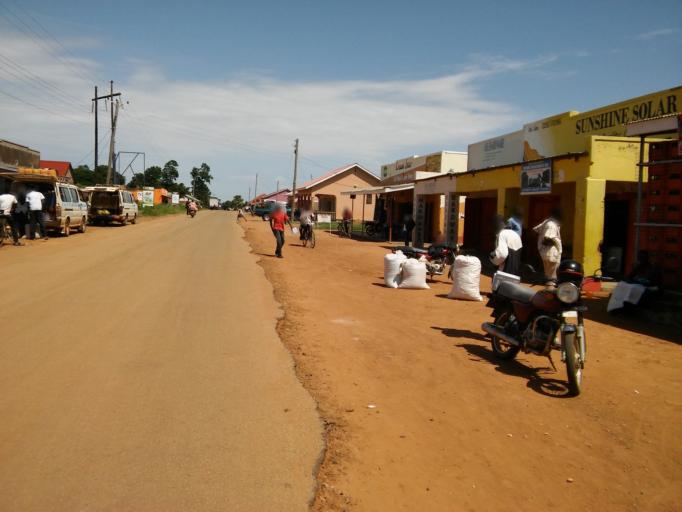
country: UG
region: Eastern Region
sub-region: Kumi District
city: Kumi
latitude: 1.4871
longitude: 33.9304
